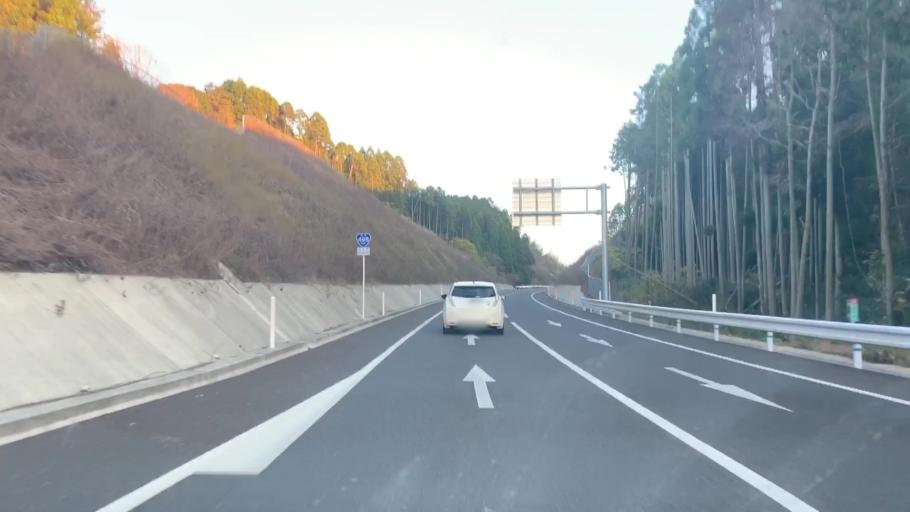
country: JP
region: Saga Prefecture
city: Takeocho-takeo
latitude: 33.2571
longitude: 129.9784
